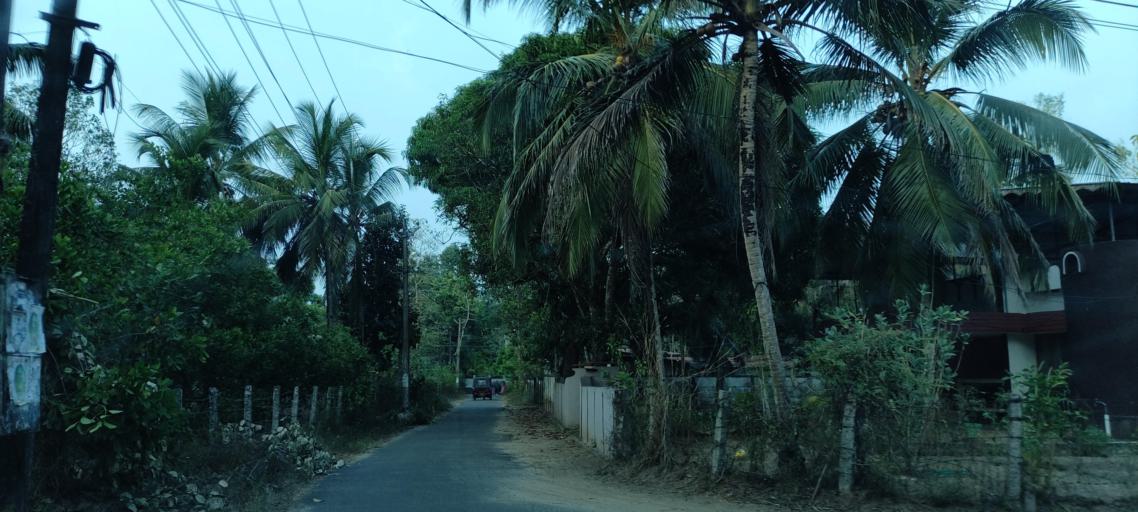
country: IN
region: Kerala
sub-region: Alappuzha
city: Mavelikara
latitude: 9.2784
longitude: 76.5508
